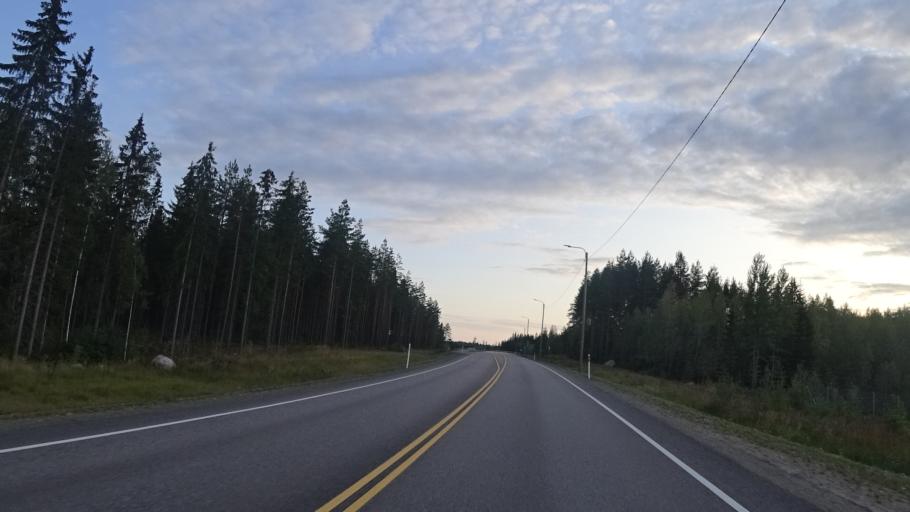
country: FI
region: Kymenlaakso
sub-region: Kotka-Hamina
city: Miehikkaelae
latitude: 60.6352
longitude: 27.8545
